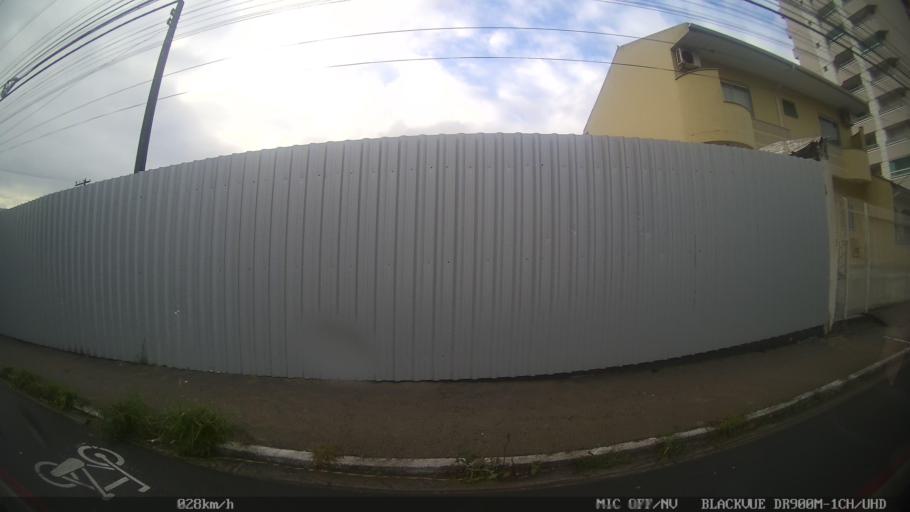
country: BR
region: Santa Catarina
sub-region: Sao Jose
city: Campinas
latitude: -27.5785
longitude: -48.6074
